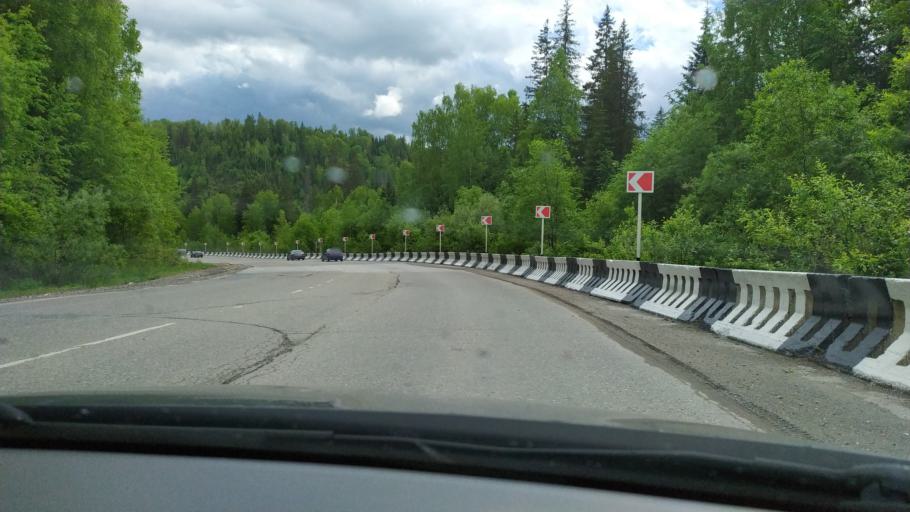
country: RU
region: Perm
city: Gremyachinsk
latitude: 58.4428
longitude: 57.8667
